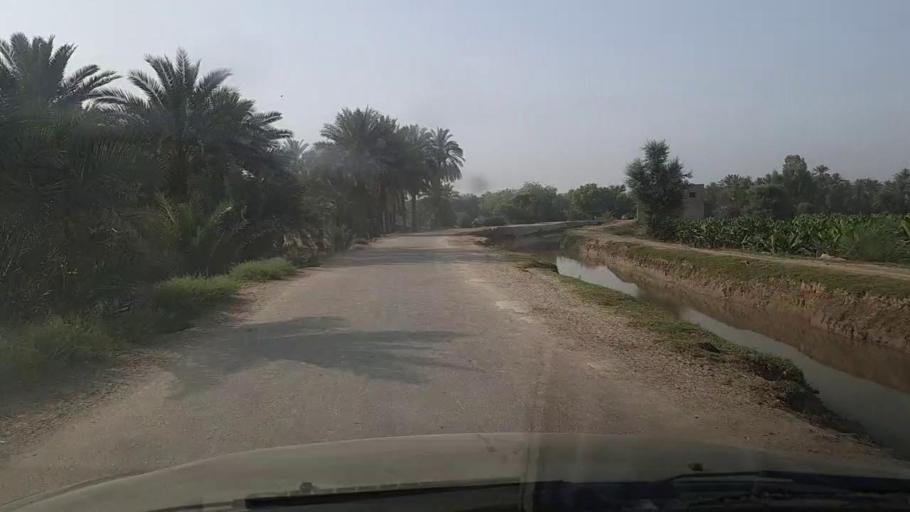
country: PK
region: Sindh
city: Pir jo Goth
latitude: 27.5583
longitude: 68.5466
